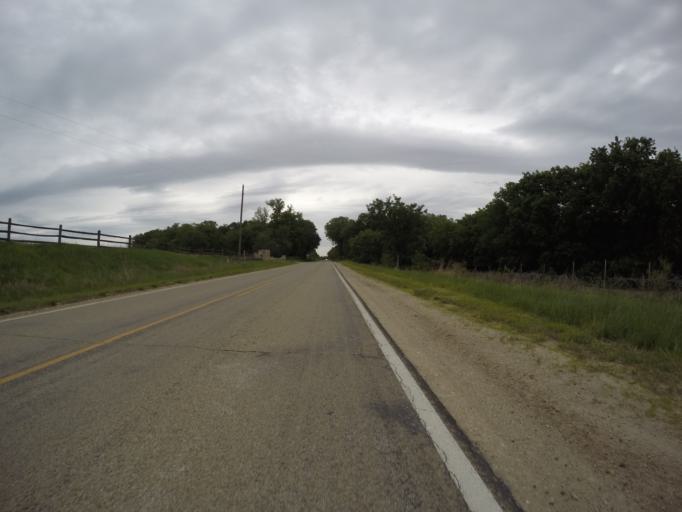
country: US
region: Kansas
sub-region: Pottawatomie County
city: Wamego
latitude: 39.1905
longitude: -96.3258
